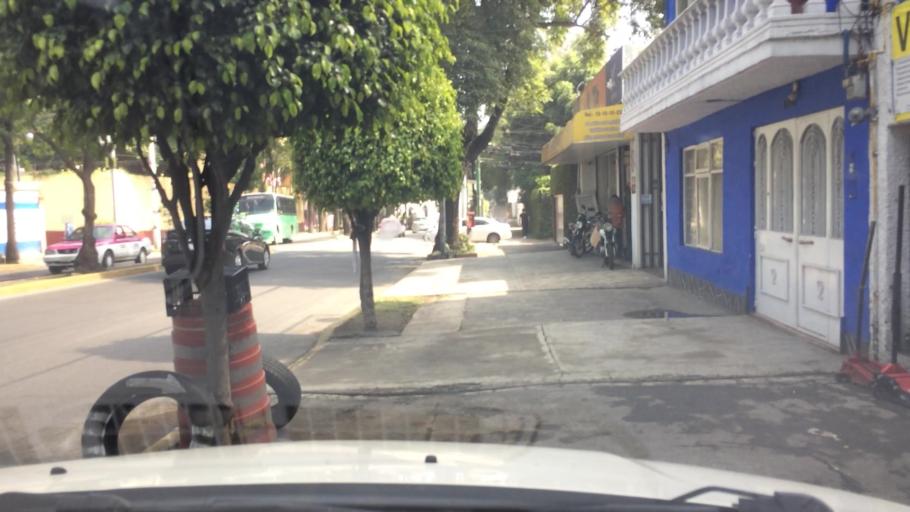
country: MX
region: Mexico City
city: Tlalpan
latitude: 19.2847
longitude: -99.1642
